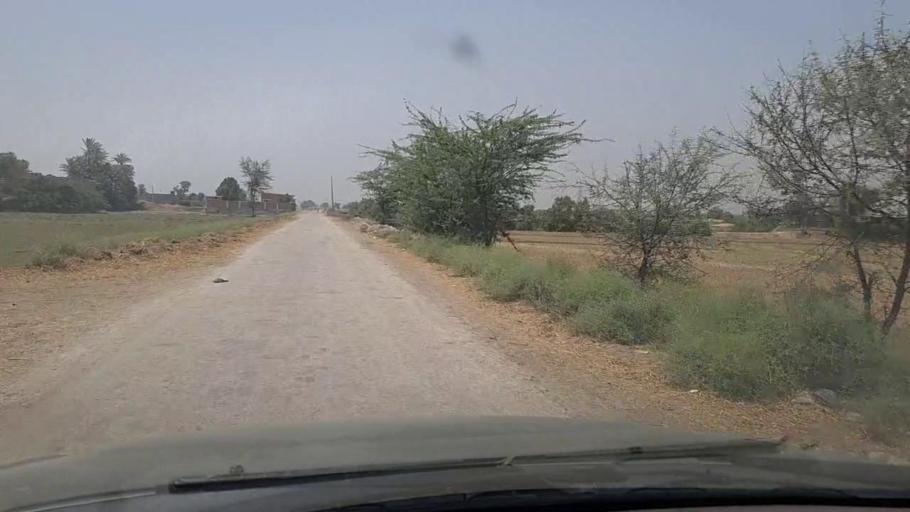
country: PK
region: Sindh
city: Ratodero
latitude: 27.7973
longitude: 68.2587
